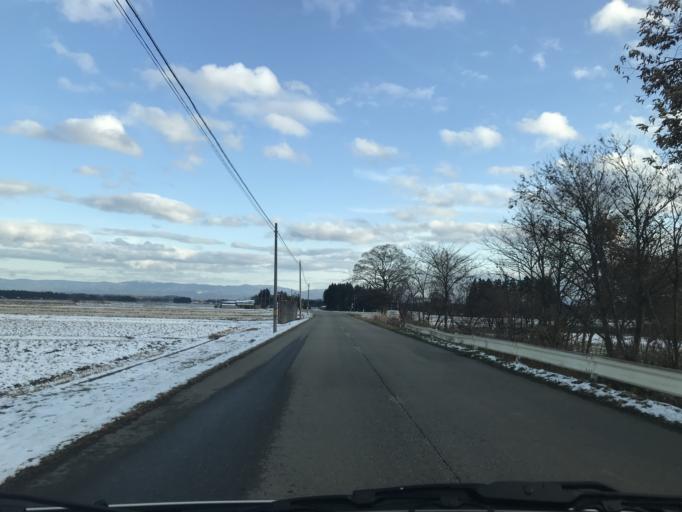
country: JP
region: Iwate
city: Kitakami
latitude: 39.2141
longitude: 141.0256
